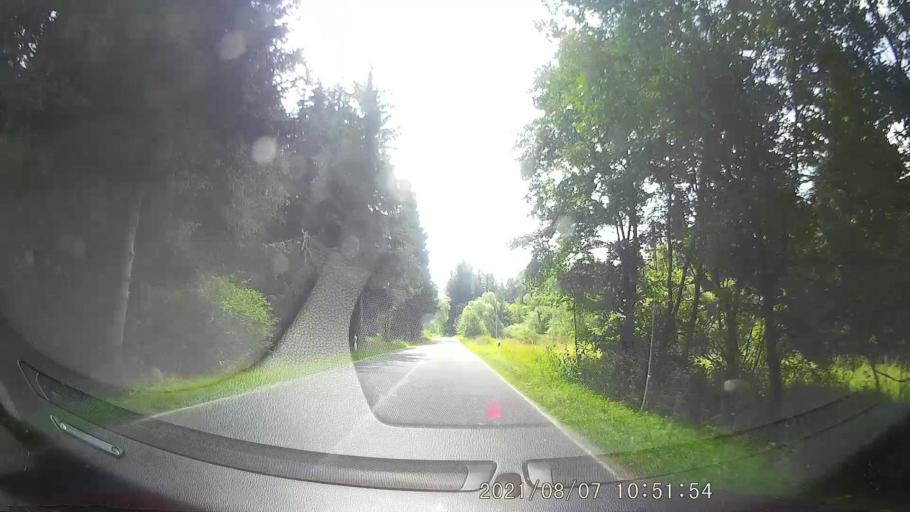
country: CZ
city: Rokytnice v Orlickych Horach
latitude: 50.2855
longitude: 16.4697
